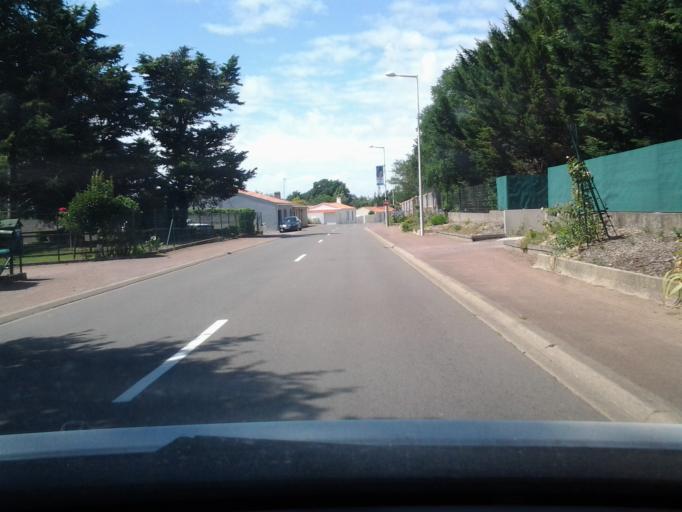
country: FR
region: Pays de la Loire
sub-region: Departement de la Vendee
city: Olonne-sur-Mer
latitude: 46.5298
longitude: -1.7566
